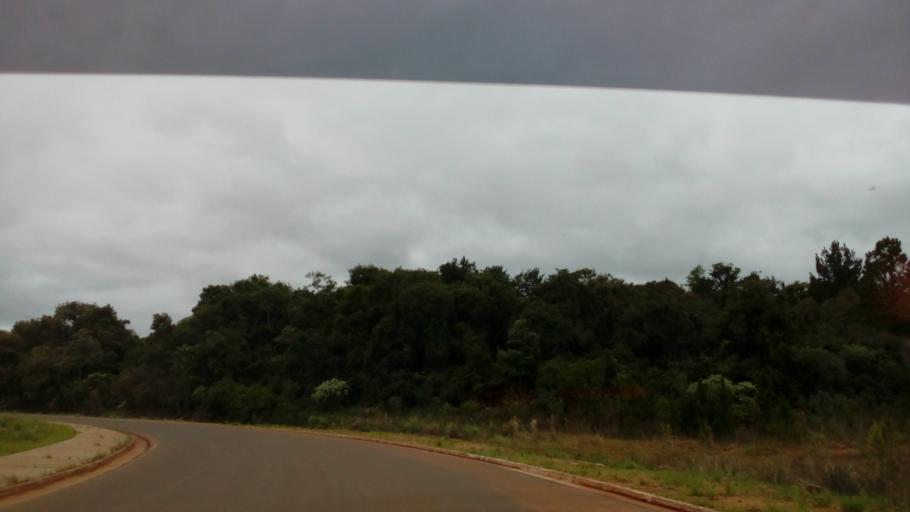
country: AR
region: Misiones
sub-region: Departamento de Candelaria
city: Candelaria
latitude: -27.4550
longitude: -55.7861
